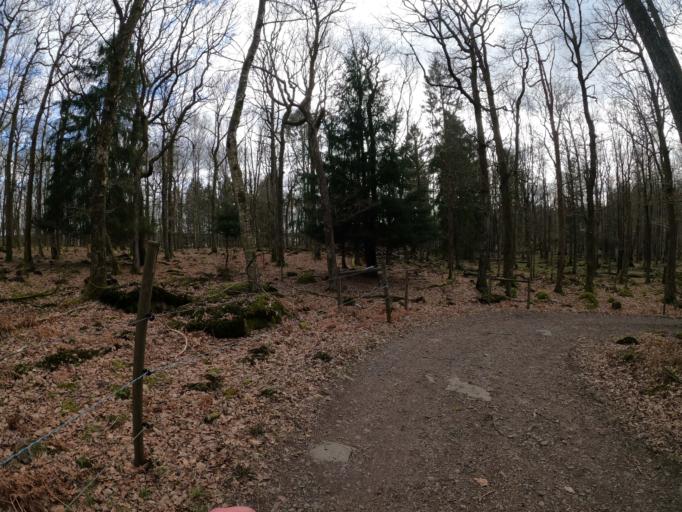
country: SE
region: Vaestra Goetaland
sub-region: Harryda Kommun
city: Molnlycke
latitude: 57.6306
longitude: 12.0937
